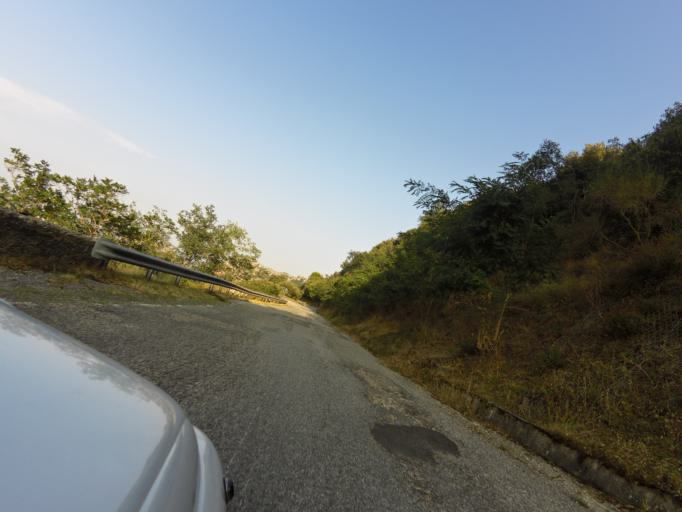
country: IT
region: Calabria
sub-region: Provincia di Reggio Calabria
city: Pazzano
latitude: 38.4679
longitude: 16.4223
